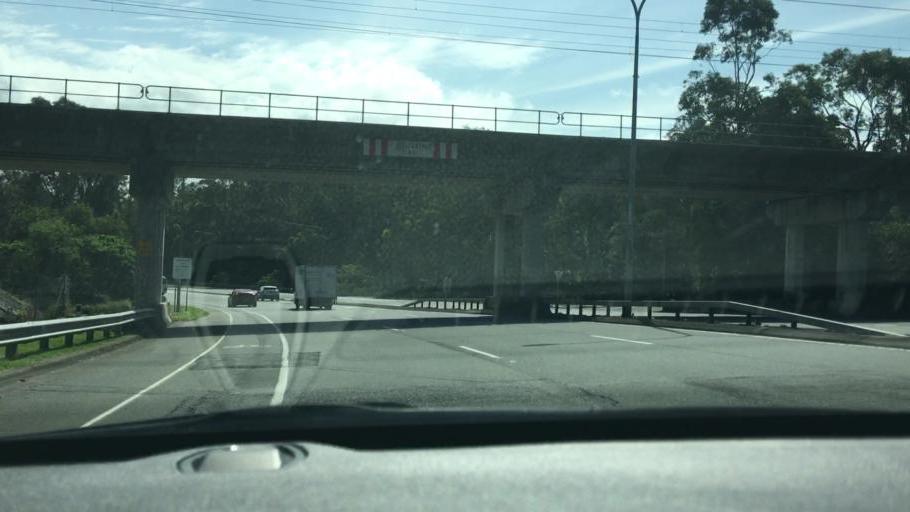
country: AU
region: Queensland
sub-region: Gold Coast
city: Nerang
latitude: -27.9819
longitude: 153.3473
